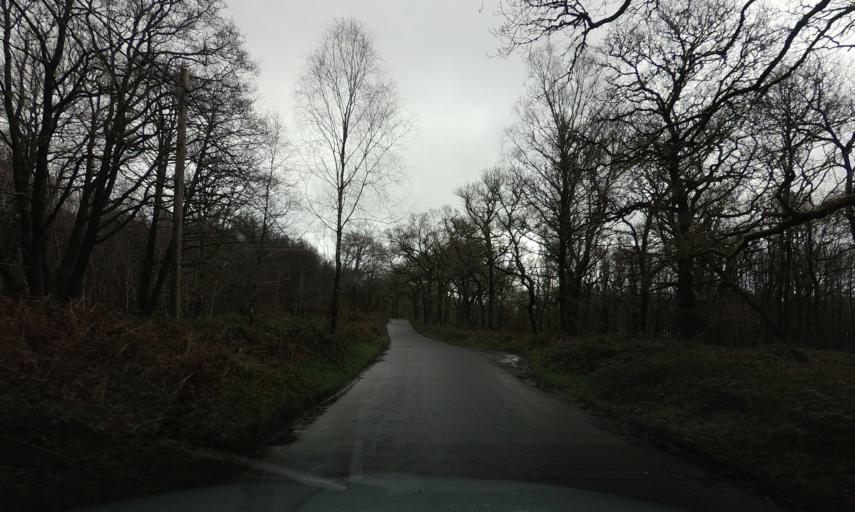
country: GB
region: Scotland
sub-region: West Dunbartonshire
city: Balloch
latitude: 56.1256
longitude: -4.6028
